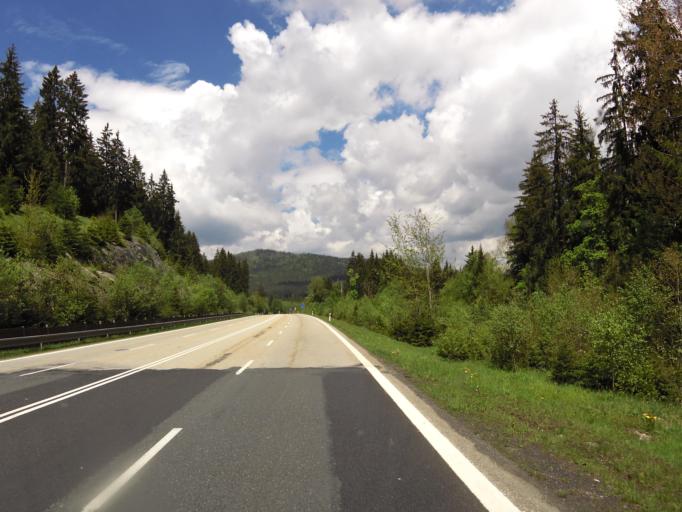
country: DE
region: Bavaria
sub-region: Lower Bavaria
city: Philippsreut
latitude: 48.8987
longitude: 13.7236
